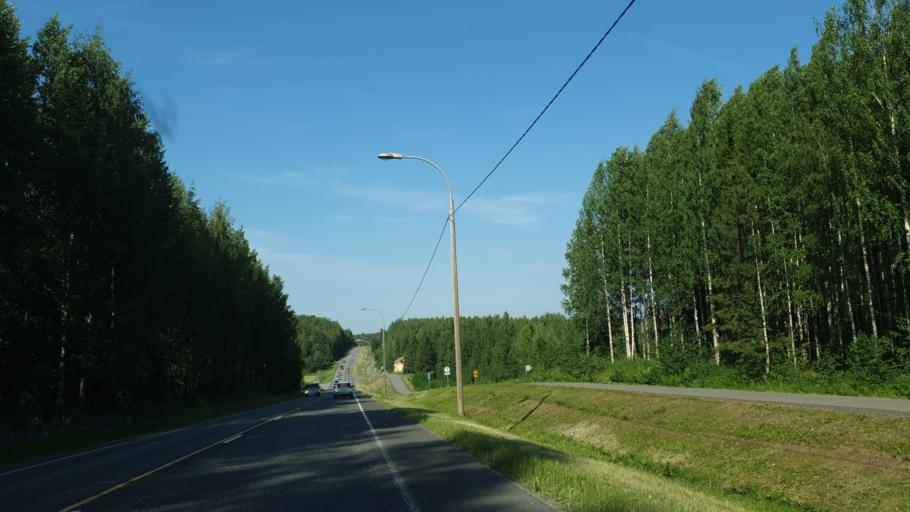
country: FI
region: Northern Savo
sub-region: Kuopio
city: Siilinjaervi
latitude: 63.1097
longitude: 27.7553
